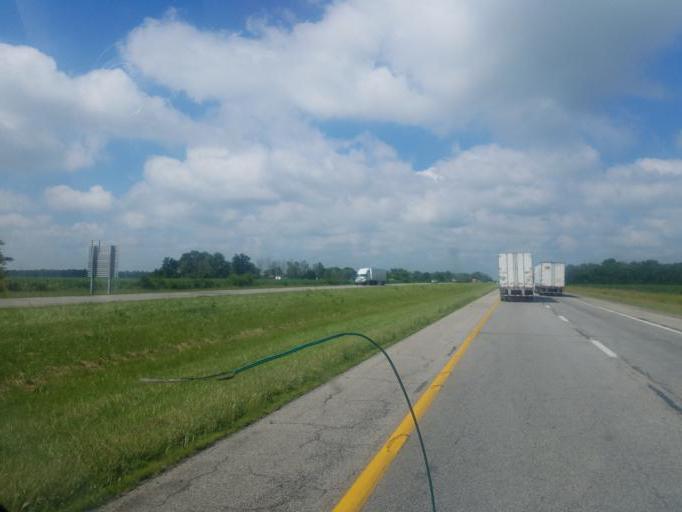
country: US
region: Ohio
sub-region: Madison County
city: Mount Sterling
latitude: 39.7531
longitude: -83.3141
